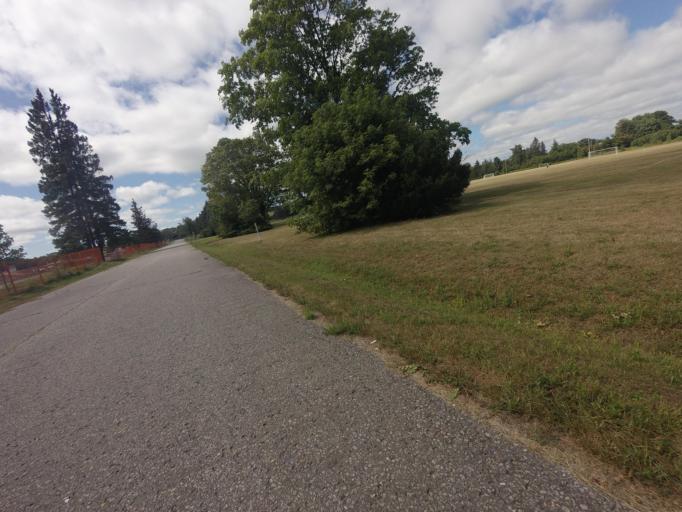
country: CA
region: Ontario
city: Uxbridge
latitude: 44.1256
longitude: -79.1248
